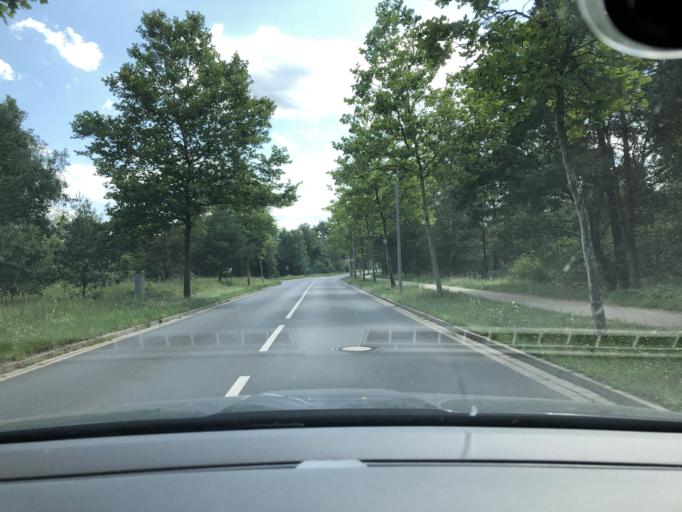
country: DE
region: Brandenburg
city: Oranienburg
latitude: 52.7696
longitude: 13.2689
